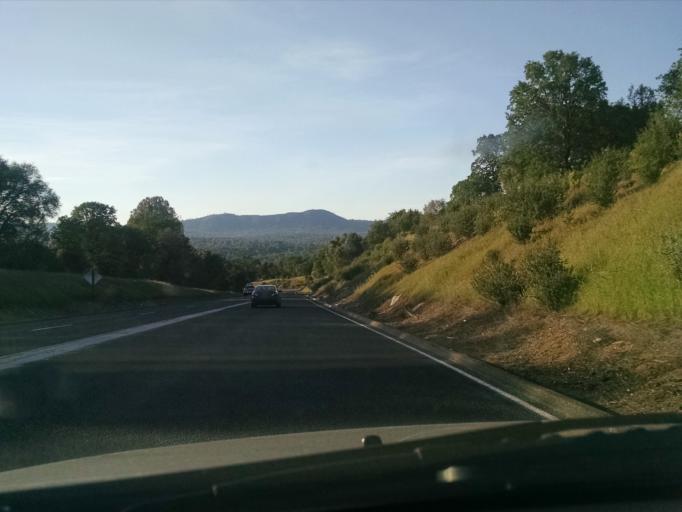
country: US
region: California
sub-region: Mariposa County
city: Mariposa
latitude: 37.4553
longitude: -119.8680
